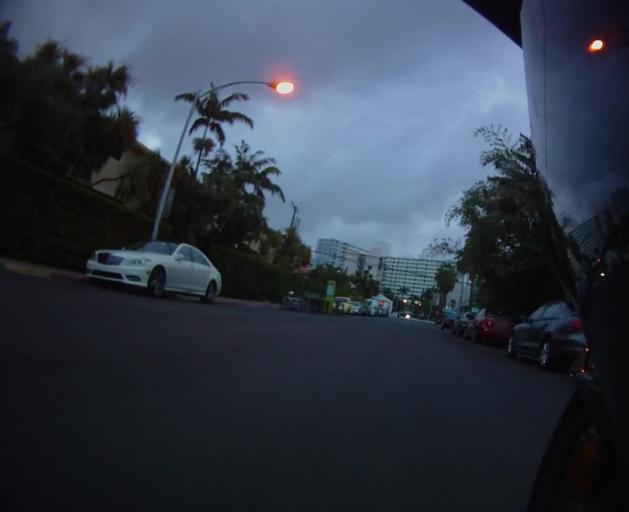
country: US
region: Florida
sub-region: Miami-Dade County
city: Miami Beach
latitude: 25.7794
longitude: -80.1398
